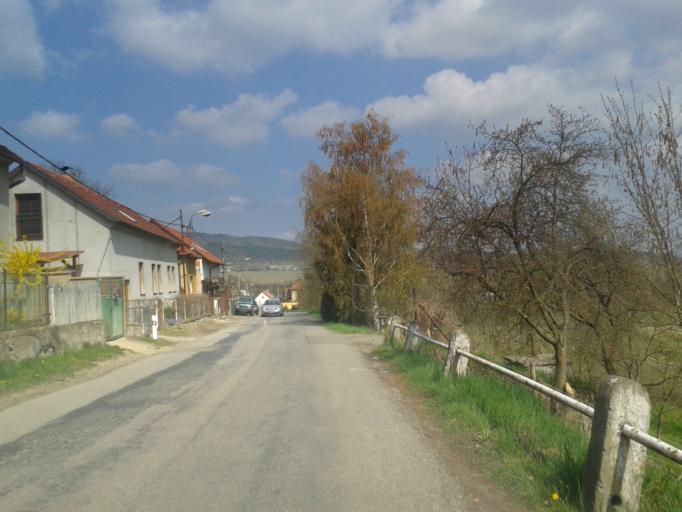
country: CZ
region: Central Bohemia
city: Zdice
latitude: 49.8968
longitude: 13.9607
